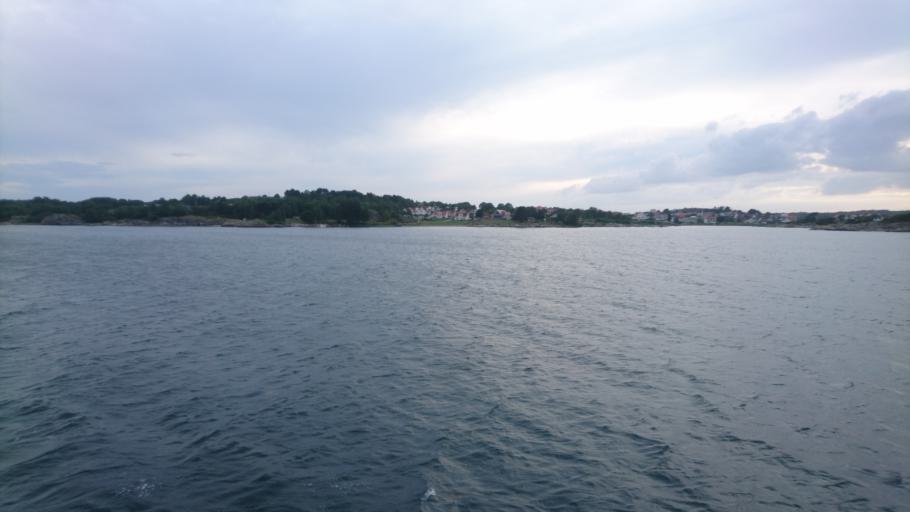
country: SE
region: Vaestra Goetaland
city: Donso
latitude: 57.5996
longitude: 11.8196
